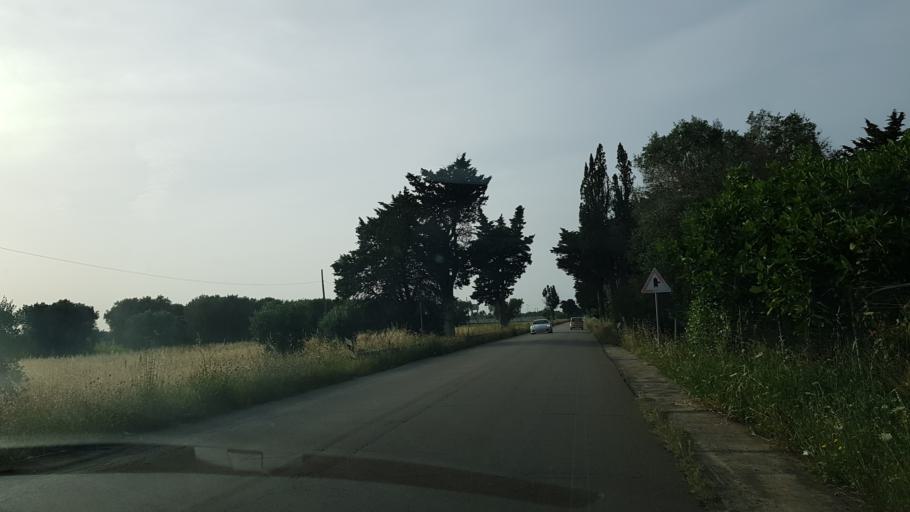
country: IT
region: Apulia
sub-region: Provincia di Brindisi
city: San Pietro Vernotico
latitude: 40.5174
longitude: 17.9874
